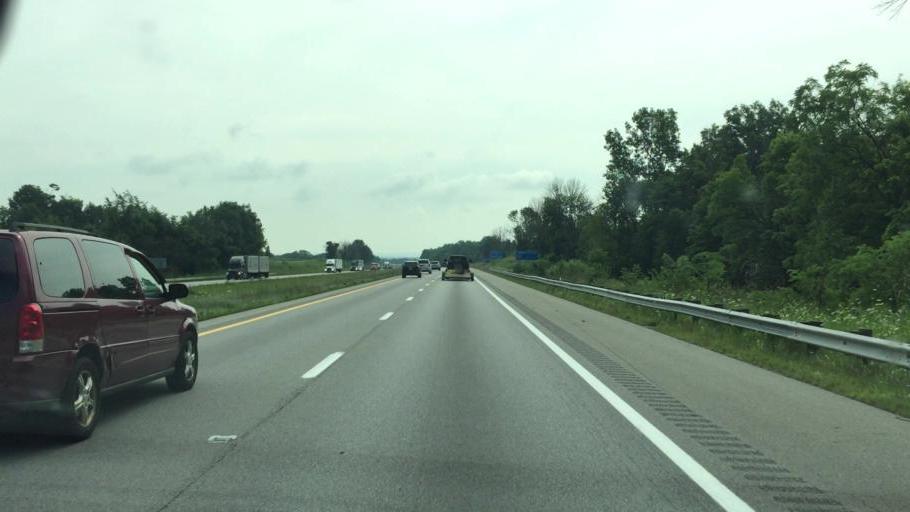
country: US
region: Ohio
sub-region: Licking County
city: Etna
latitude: 39.9456
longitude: -82.6196
